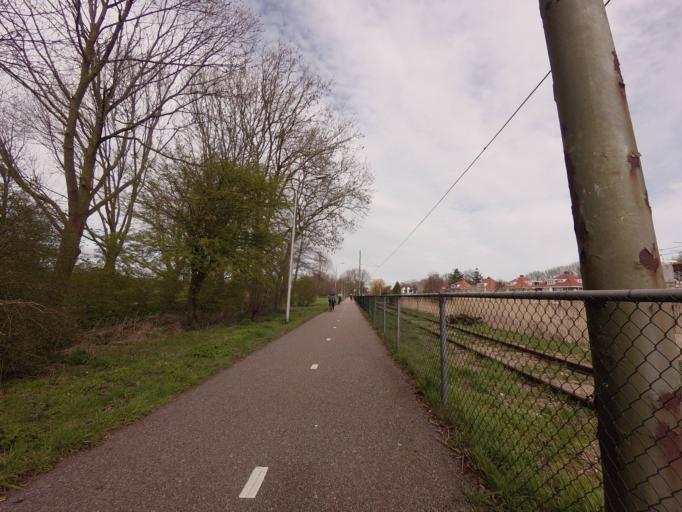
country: NL
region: North Holland
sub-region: Gemeente Amstelveen
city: Amstelveen
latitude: 52.2971
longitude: 4.8433
